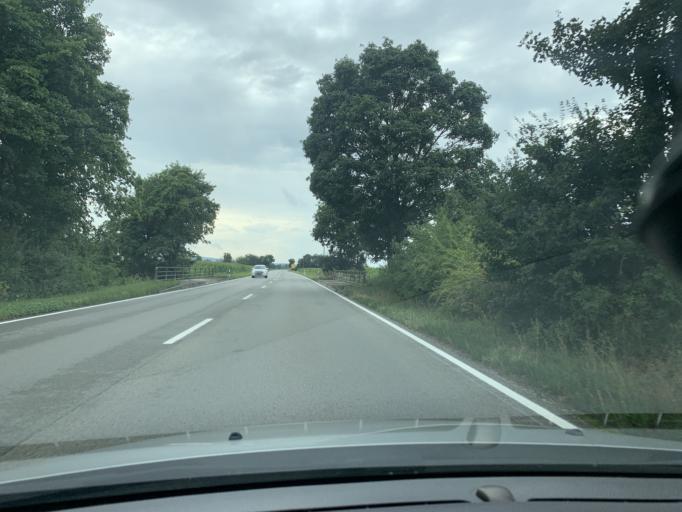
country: DE
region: Bavaria
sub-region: Upper Bavaria
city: Neufahrn
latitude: 48.2512
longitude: 12.4468
